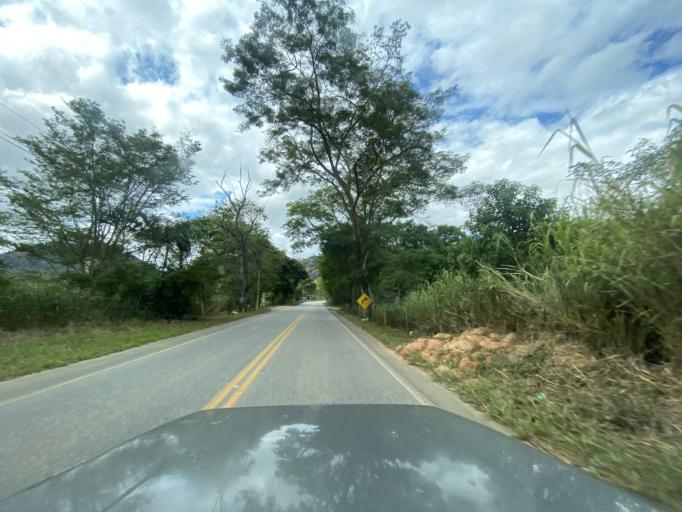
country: BR
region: Espirito Santo
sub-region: Jeronimo Monteiro
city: Jeronimo Monteiro
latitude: -20.7687
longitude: -41.4331
